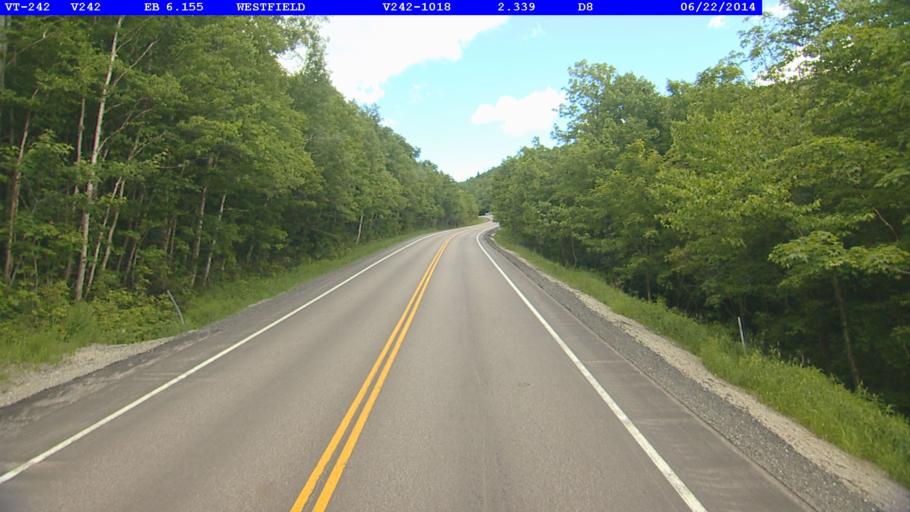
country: US
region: Vermont
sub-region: Franklin County
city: Richford
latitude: 44.9113
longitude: -72.5072
